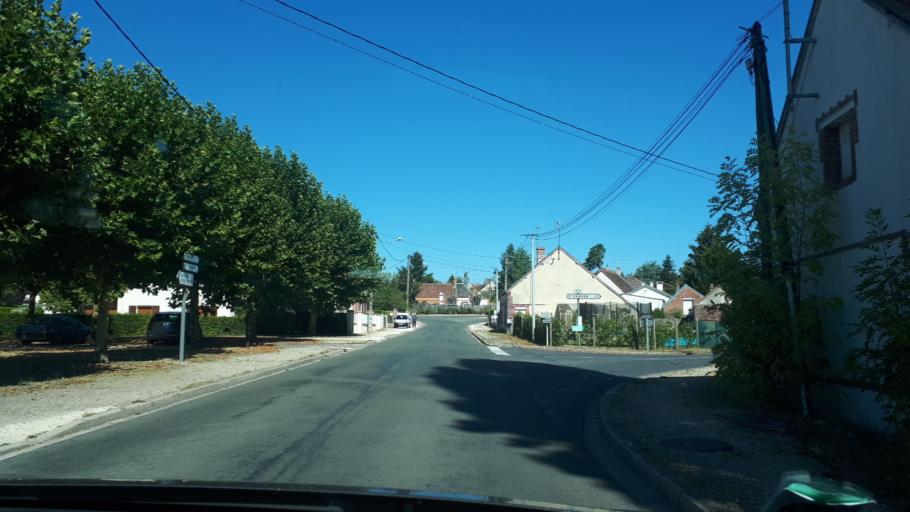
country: FR
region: Centre
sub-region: Departement du Loiret
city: Coullons
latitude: 47.6243
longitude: 2.4910
